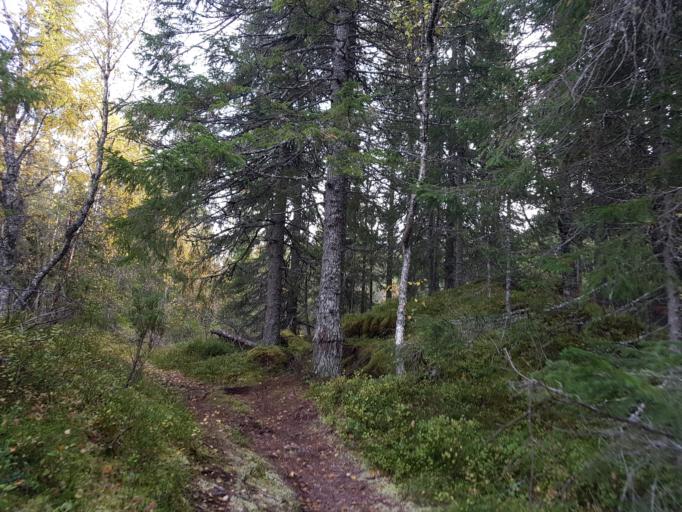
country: NO
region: Sor-Trondelag
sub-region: Trondheim
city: Trondheim
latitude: 63.4462
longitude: 10.2776
